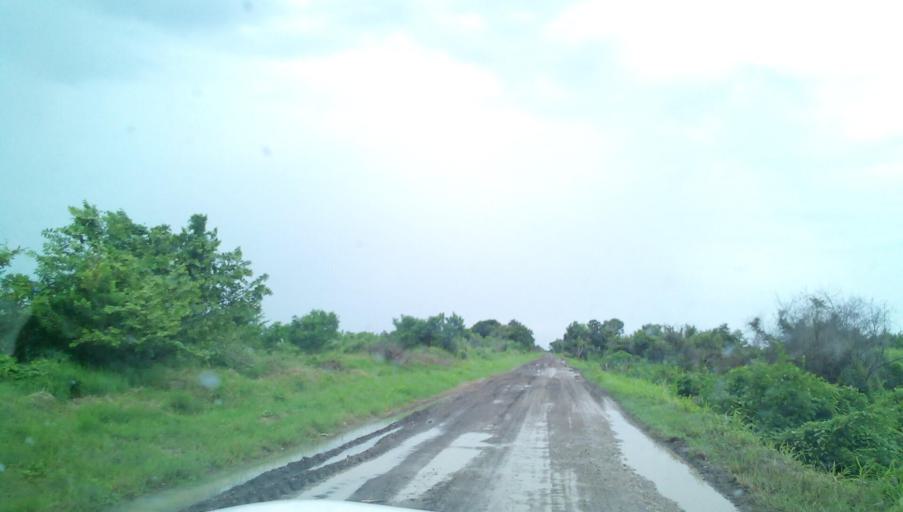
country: MX
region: Veracruz
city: Panuco
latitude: 21.8140
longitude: -98.1111
